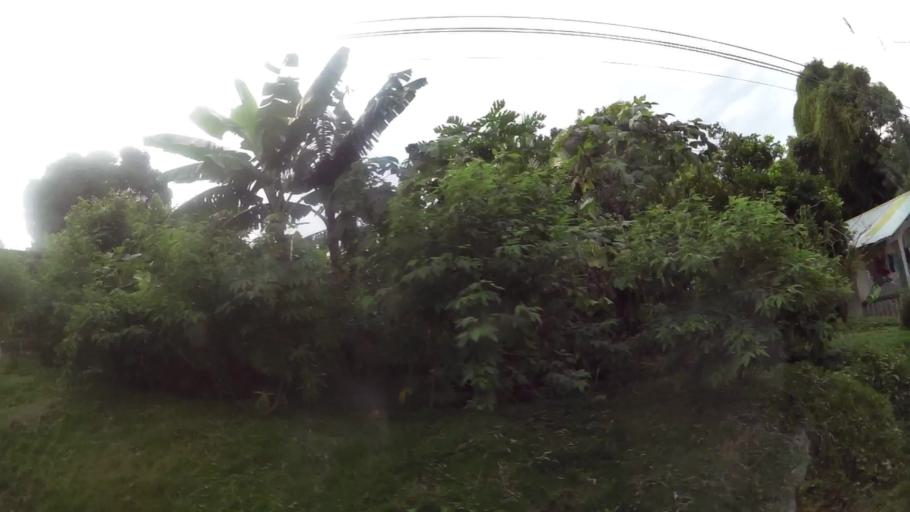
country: PA
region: Panama
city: Guadalupe
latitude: 8.8604
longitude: -79.8145
